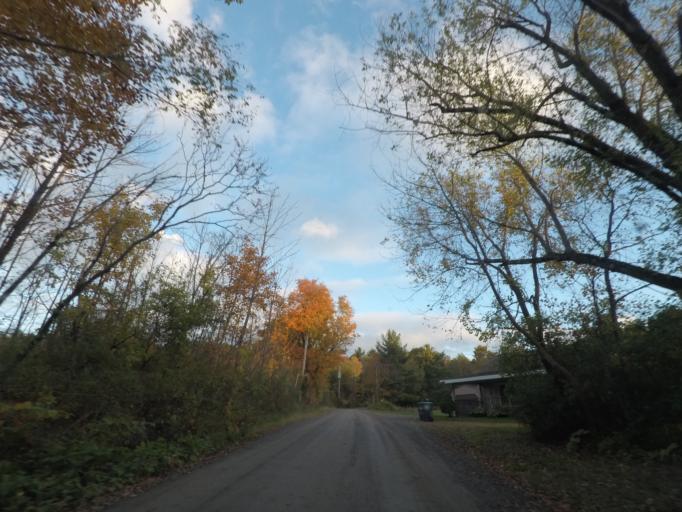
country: US
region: New York
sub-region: Rensselaer County
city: Nassau
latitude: 42.5165
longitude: -73.5927
